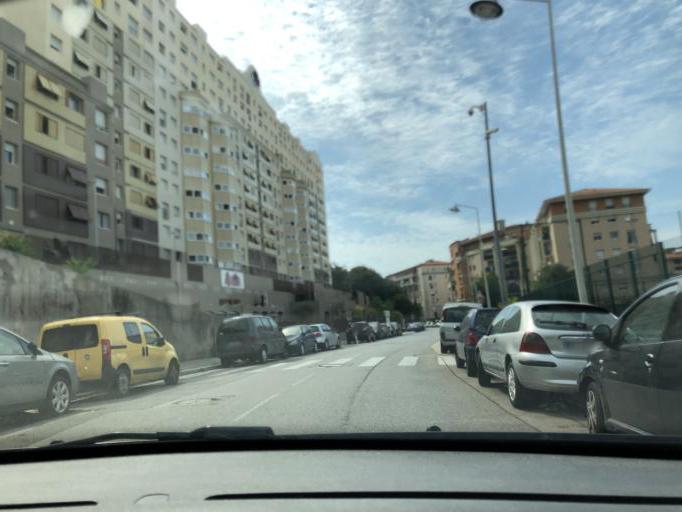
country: FR
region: Provence-Alpes-Cote d'Azur
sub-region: Departement des Alpes-Maritimes
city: Saint-Andre-de-la-Roche
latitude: 43.7205
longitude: 7.2938
